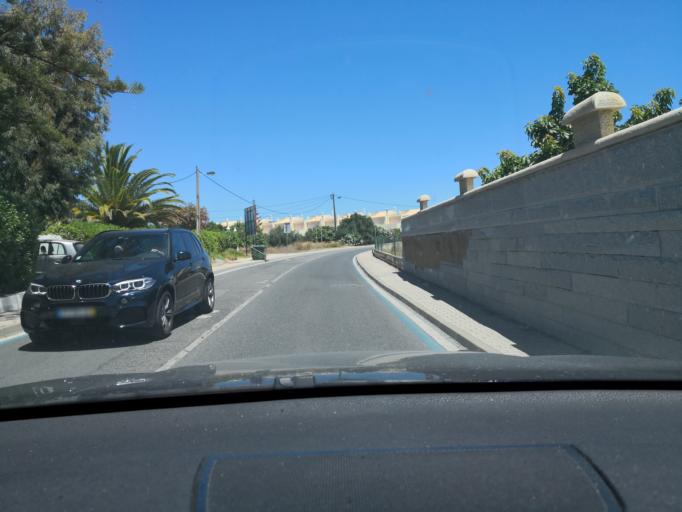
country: PT
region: Faro
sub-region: Albufeira
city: Ferreiras
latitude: 37.1006
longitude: -8.2168
